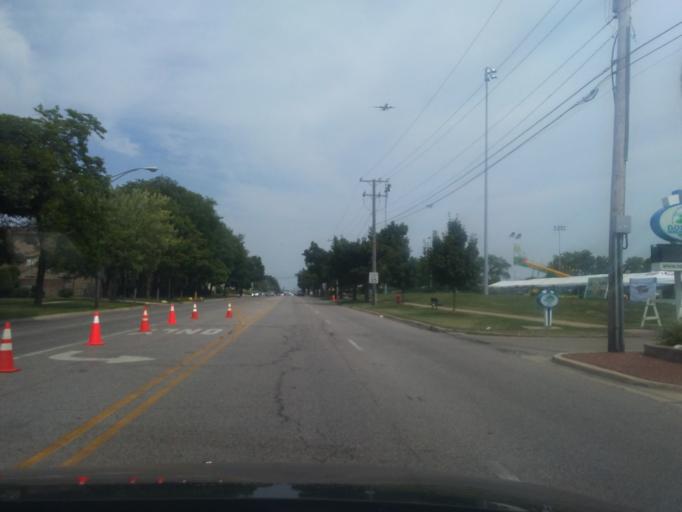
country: US
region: Illinois
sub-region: Cook County
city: Norridge
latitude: 41.9669
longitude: -87.8193
